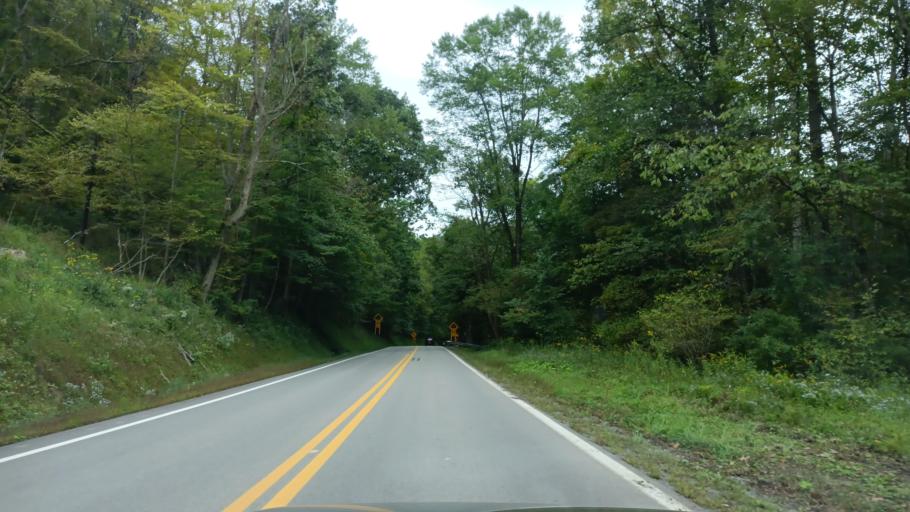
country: US
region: West Virginia
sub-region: Taylor County
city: Grafton
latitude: 39.3378
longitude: -79.9333
